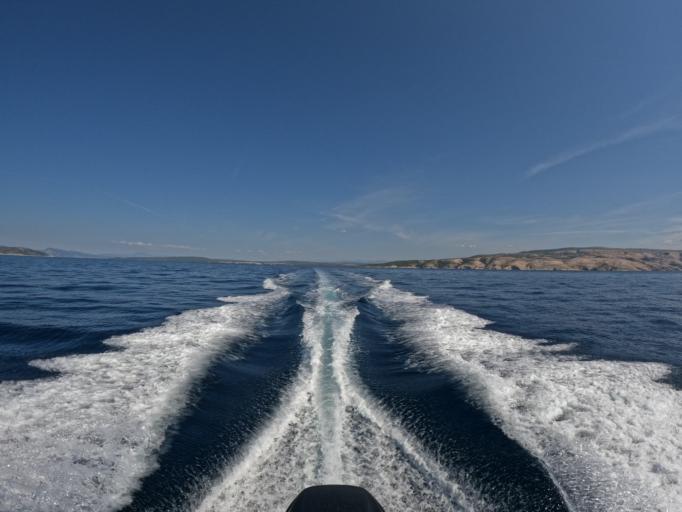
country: HR
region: Primorsko-Goranska
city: Punat
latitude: 44.9415
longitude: 14.6157
